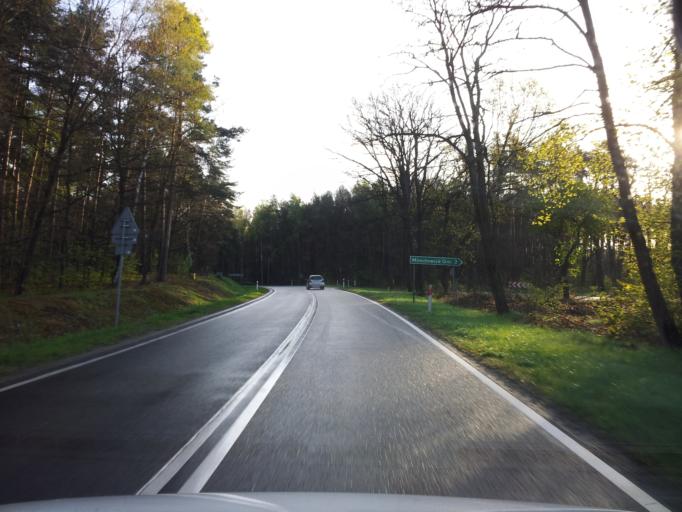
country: PL
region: Lubusz
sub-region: Powiat zarski
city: Sieniawa Zarska
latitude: 51.5835
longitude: 15.0758
